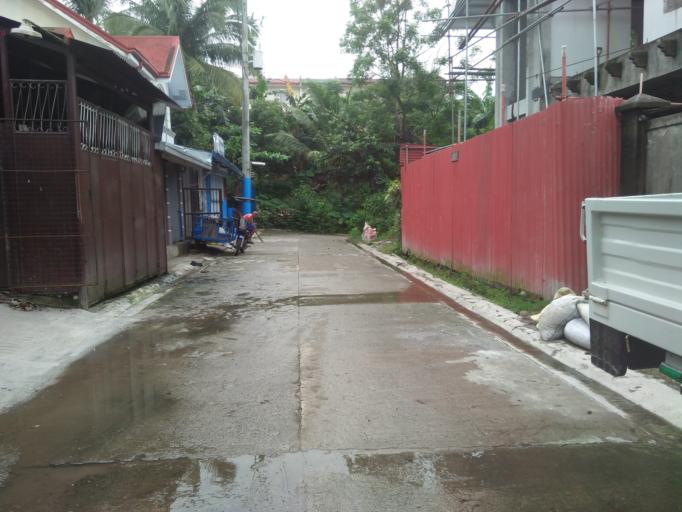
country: PH
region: Central Luzon
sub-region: Province of Bulacan
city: San Jose del Monte
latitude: 14.7482
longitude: 121.0640
